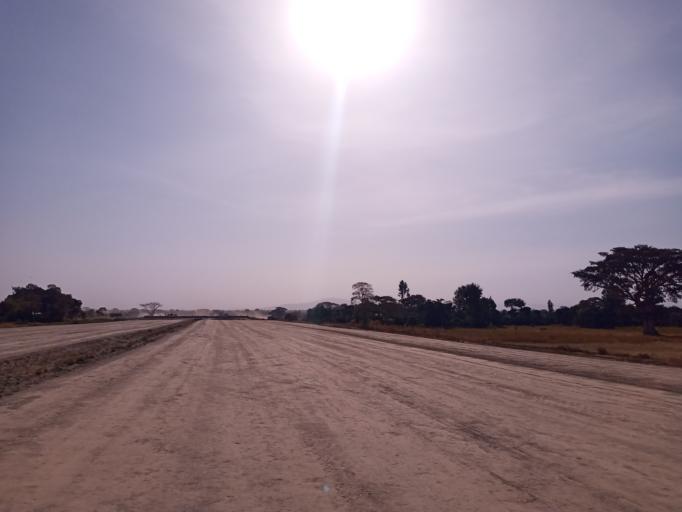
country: ET
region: Oromiya
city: Shashemene
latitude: 7.3109
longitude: 38.6236
